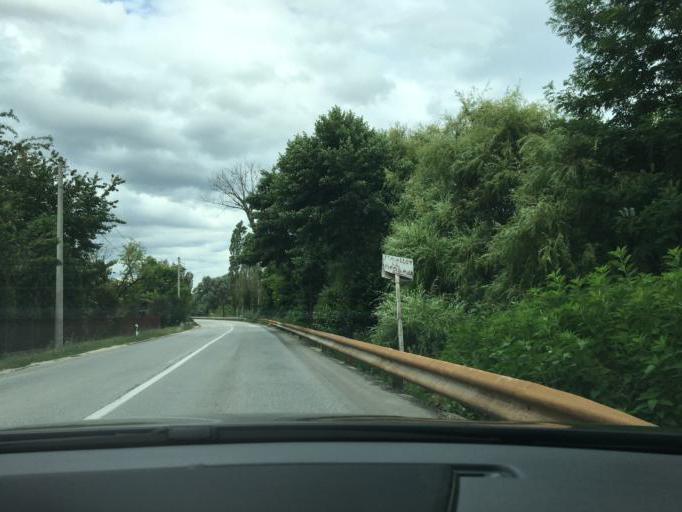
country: MK
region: Opstina Rankovce
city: Rankovce
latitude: 42.1723
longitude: 22.2055
